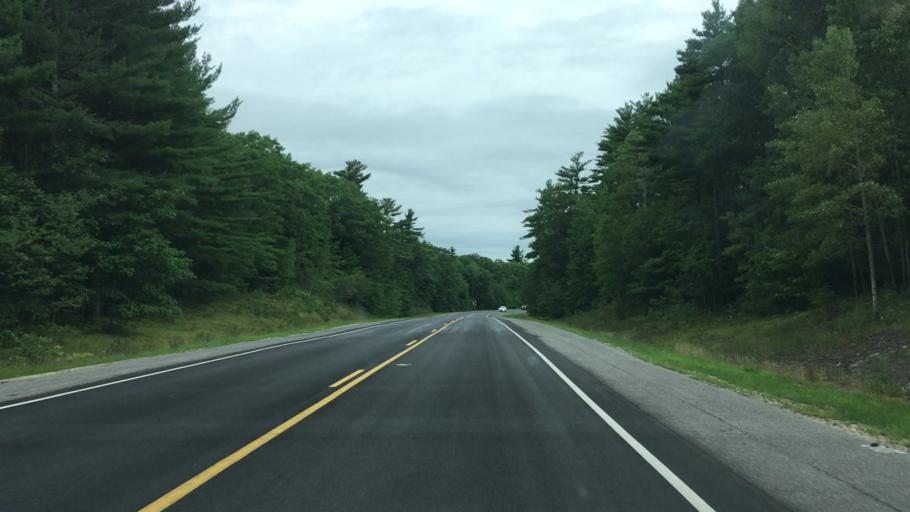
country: US
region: Maine
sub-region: Washington County
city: Cherryfield
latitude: 44.9050
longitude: -67.8566
